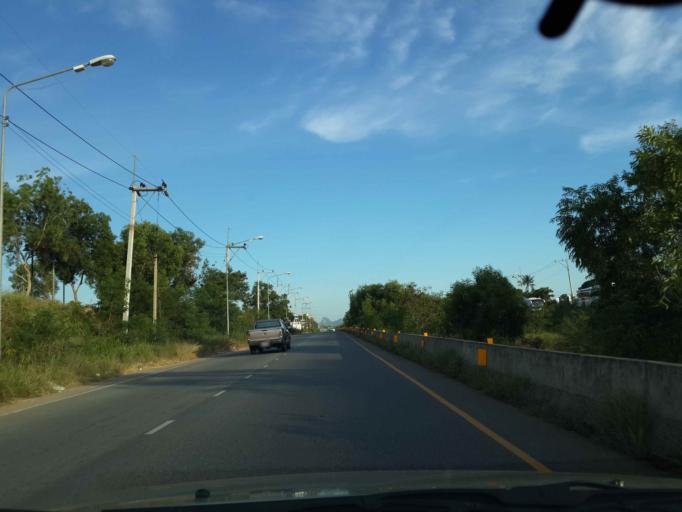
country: TH
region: Chon Buri
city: Phatthaya
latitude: 12.8667
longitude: 100.9111
